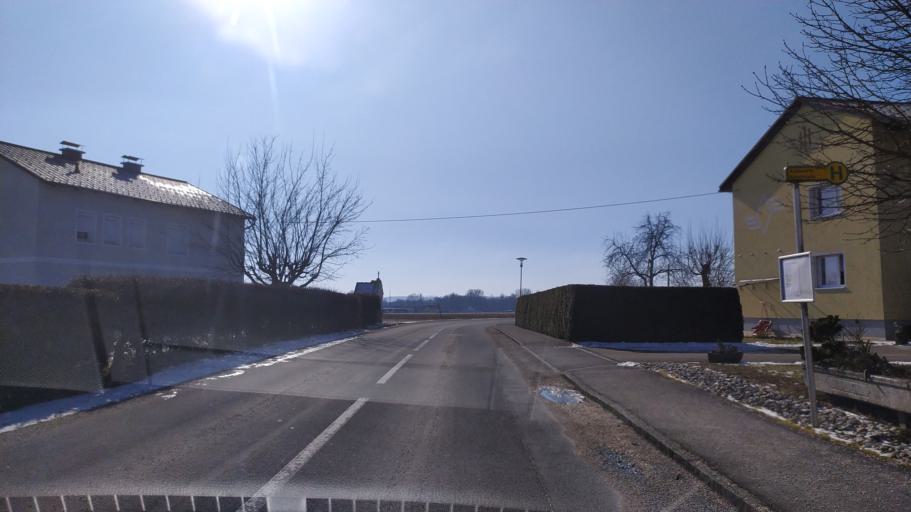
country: AT
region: Upper Austria
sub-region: Politischer Bezirk Urfahr-Umgebung
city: Goldworth
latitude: 48.3306
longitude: 14.1063
